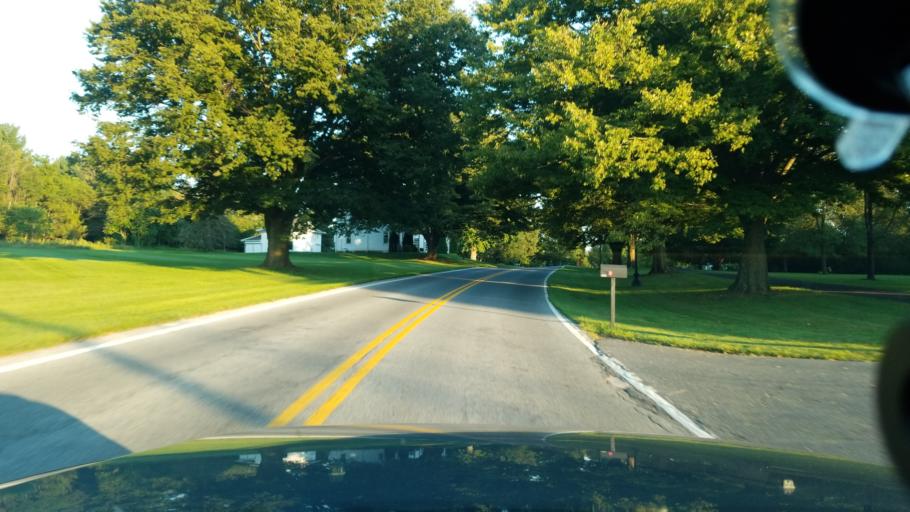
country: US
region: Pennsylvania
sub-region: Dauphin County
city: Hershey
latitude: 40.2825
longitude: -76.6348
